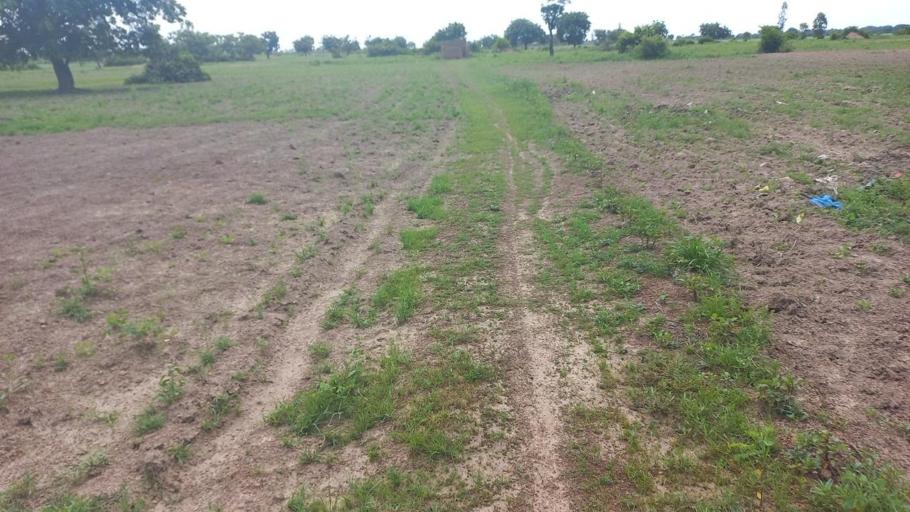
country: ML
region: Koulikoro
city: Dioila
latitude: 12.7637
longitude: -6.9250
